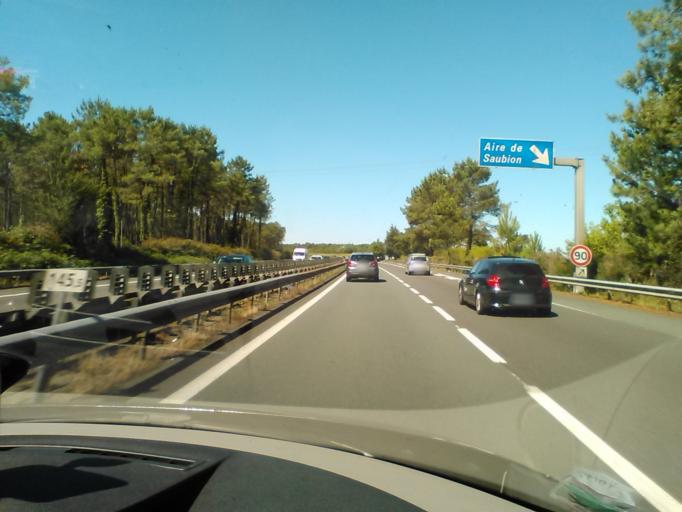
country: FR
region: Aquitaine
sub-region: Departement des Landes
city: Saint-Vincent-de-Tyrosse
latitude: 43.6806
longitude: -1.2993
